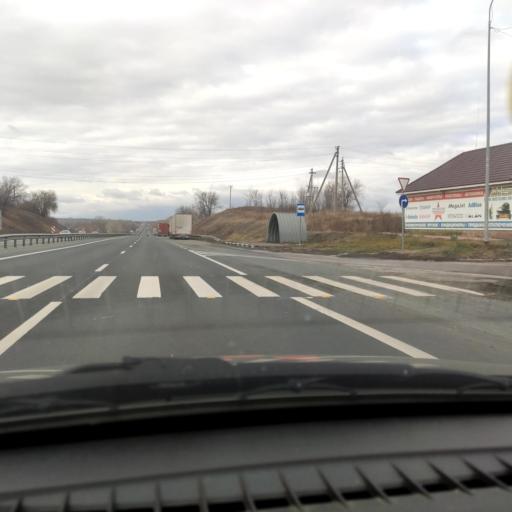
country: RU
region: Samara
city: Novosemeykino
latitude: 53.4217
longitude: 50.3251
